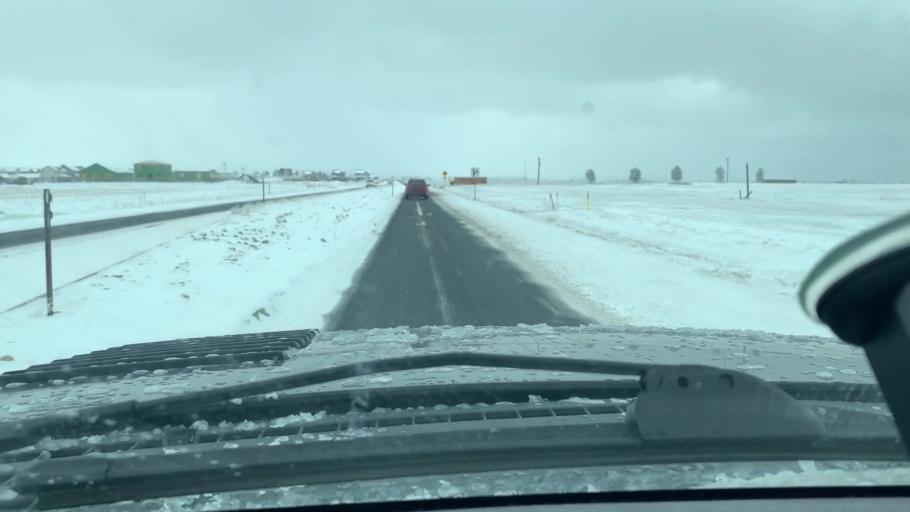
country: US
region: Colorado
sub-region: Weld County
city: Mead
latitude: 40.1922
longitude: -104.9702
